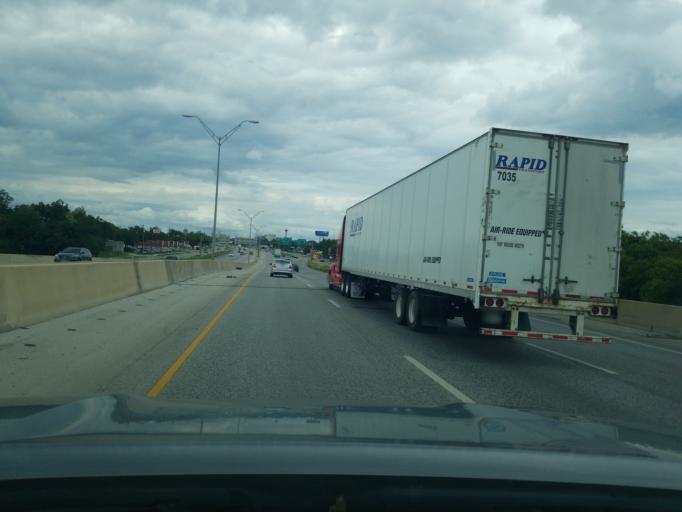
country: US
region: Texas
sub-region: Bexar County
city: San Antonio
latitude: 29.3687
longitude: -98.5181
